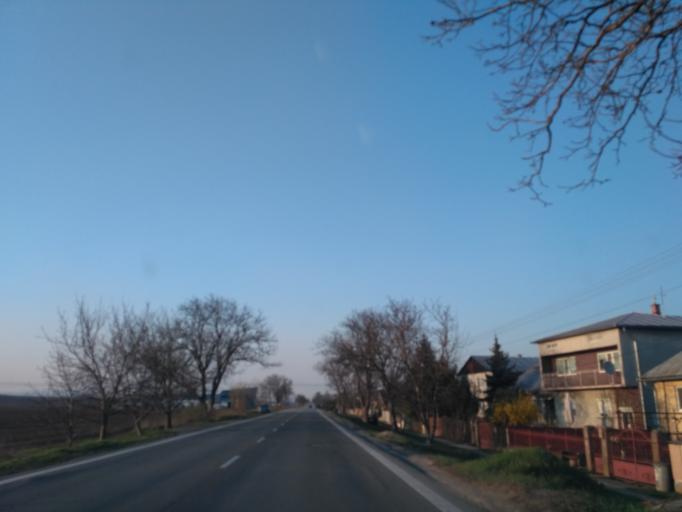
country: HU
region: Borsod-Abauj-Zemplen
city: Gonc
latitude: 48.5725
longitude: 21.2576
